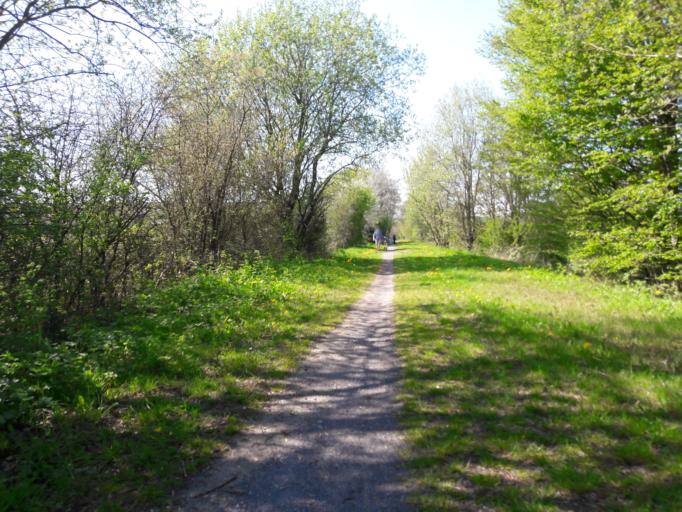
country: FR
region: Nord-Pas-de-Calais
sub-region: Departement du Nord
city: Sains-du-Nord
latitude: 50.1777
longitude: 4.0770
